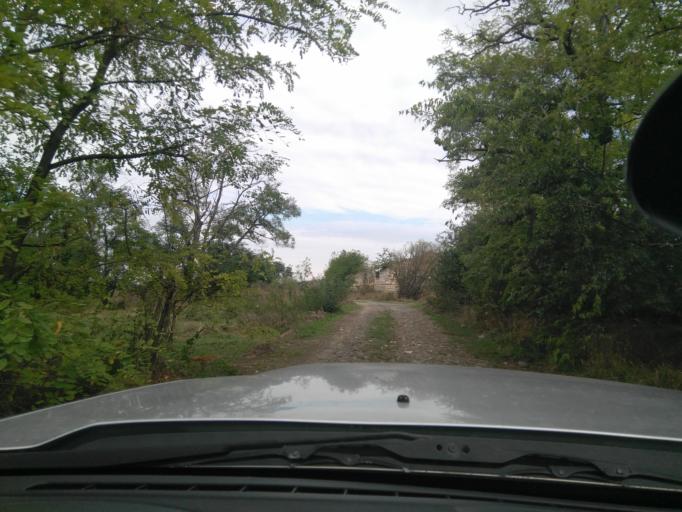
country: HU
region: Fejer
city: Val
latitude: 47.3831
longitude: 18.7393
